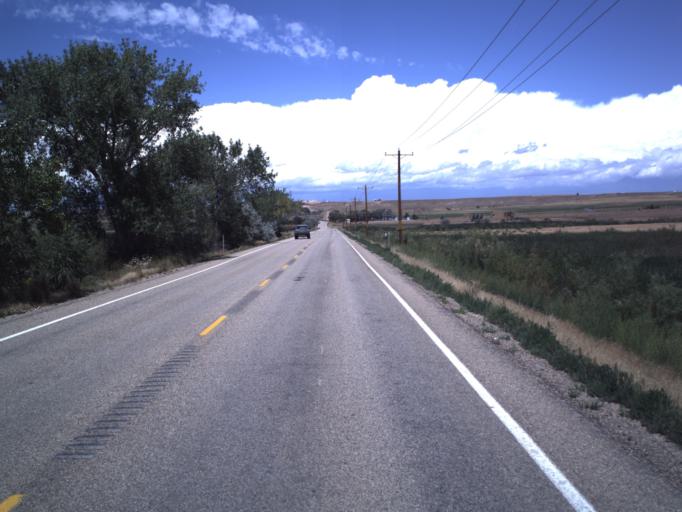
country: US
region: Utah
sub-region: Uintah County
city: Naples
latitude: 40.1948
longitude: -109.6647
